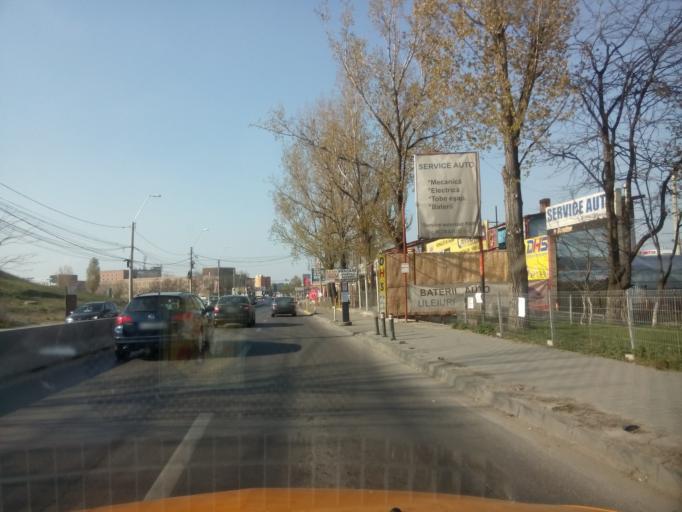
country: RO
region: Ilfov
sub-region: Comuna Popesti-Leordeni
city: Popesti-Leordeni
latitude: 44.4014
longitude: 26.1426
